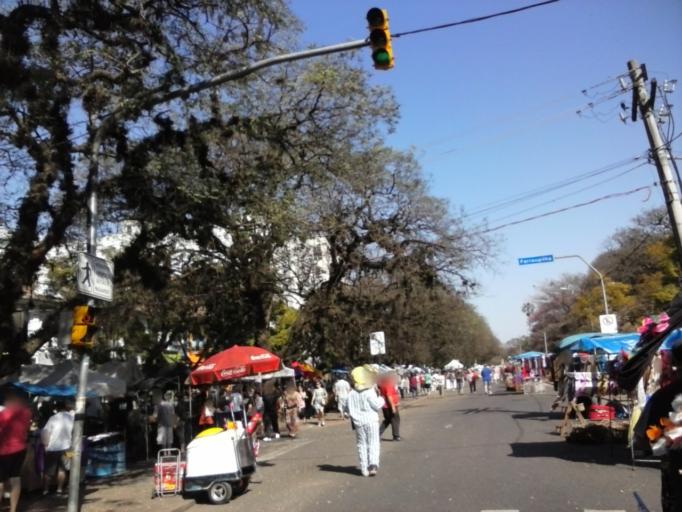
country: BR
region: Rio Grande do Sul
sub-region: Porto Alegre
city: Porto Alegre
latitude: -30.0369
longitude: -51.2115
